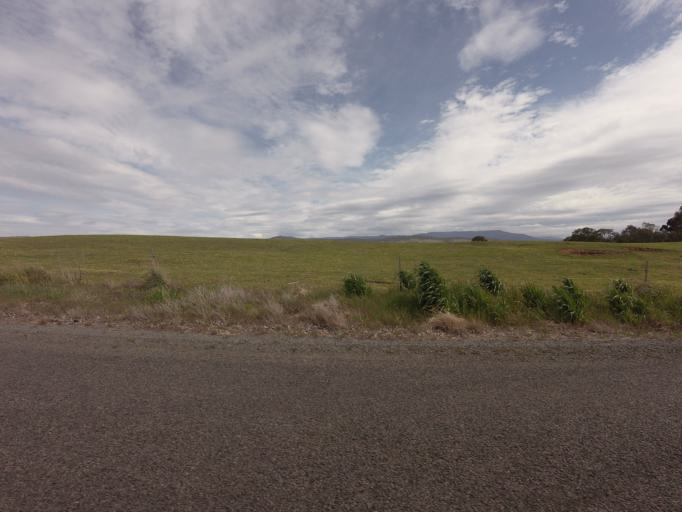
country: AU
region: Tasmania
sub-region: Northern Midlands
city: Evandale
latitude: -41.8843
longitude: 147.3664
